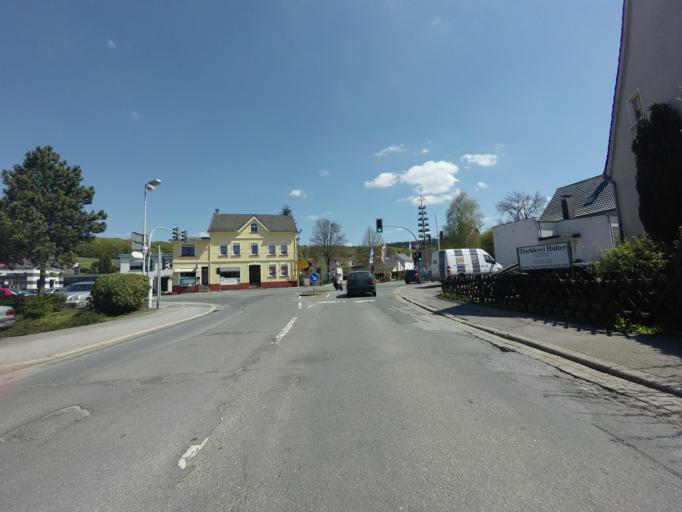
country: DE
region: North Rhine-Westphalia
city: Iserlohn
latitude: 51.3302
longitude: 7.7357
